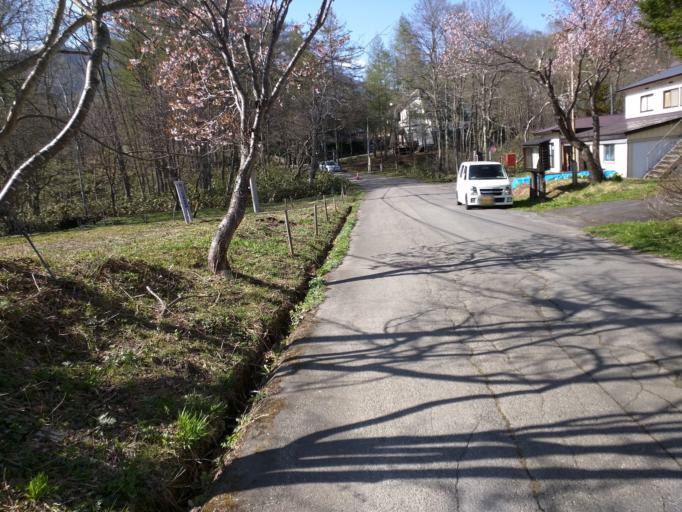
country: JP
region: Nagano
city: Nagano-shi
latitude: 36.7491
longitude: 138.0812
